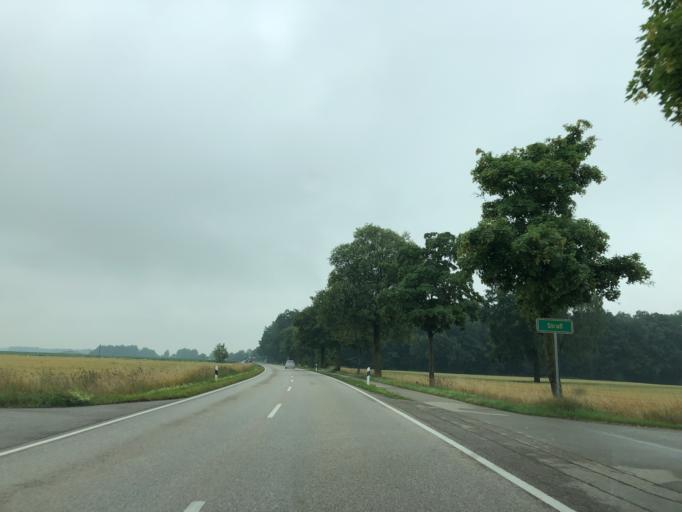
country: DE
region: Bavaria
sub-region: Upper Bavaria
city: Worth
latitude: 48.2655
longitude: 11.9232
